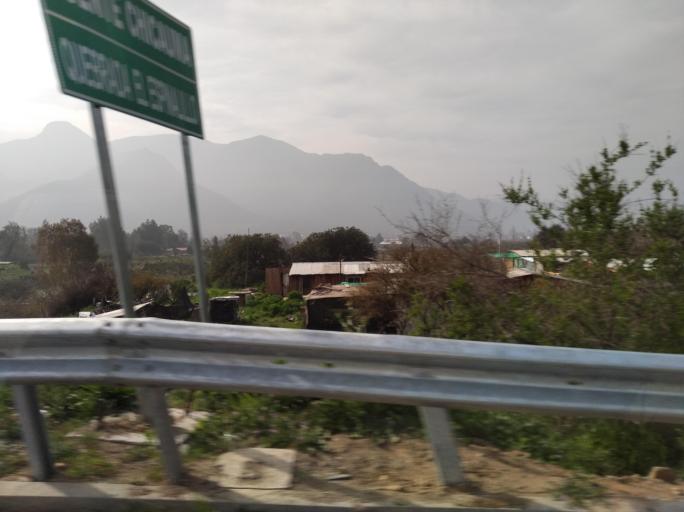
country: CL
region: Santiago Metropolitan
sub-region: Provincia de Chacabuco
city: Lampa
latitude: -33.2365
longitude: -70.9259
